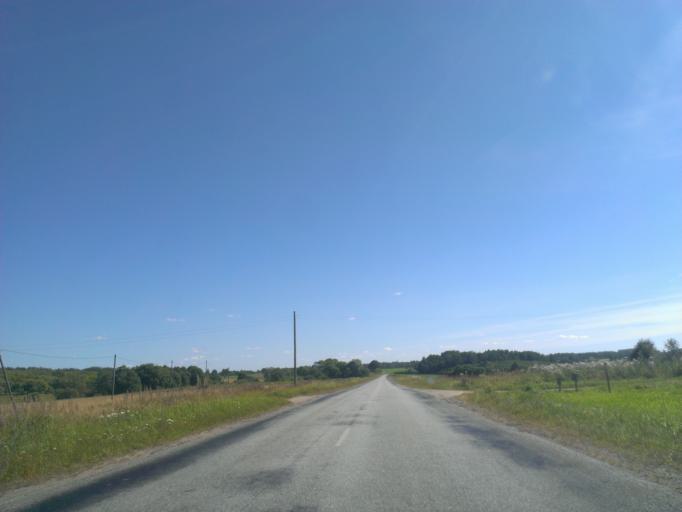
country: LV
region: Malpils
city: Malpils
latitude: 57.0193
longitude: 24.8533
